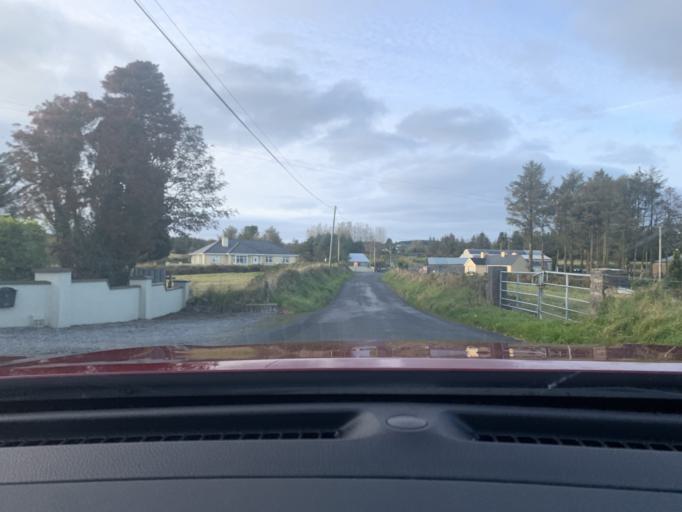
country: IE
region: Connaught
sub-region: Roscommon
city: Ballaghaderreen
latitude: 53.9154
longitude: -8.5901
